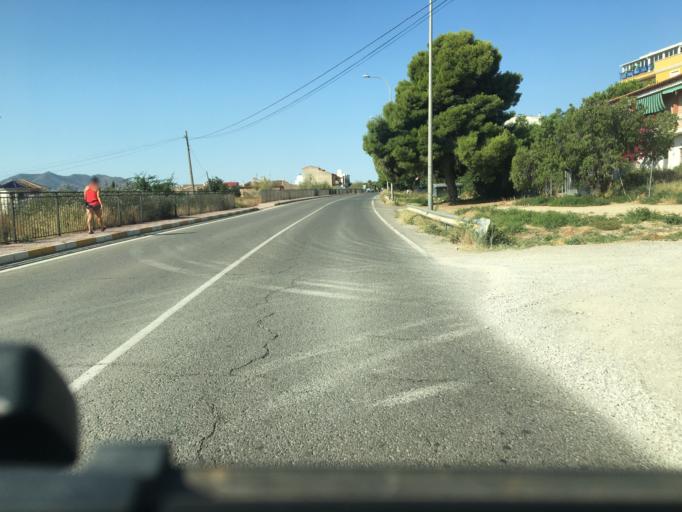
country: ES
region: Murcia
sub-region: Murcia
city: Puerto Lumbreras
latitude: 37.5547
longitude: -1.8109
